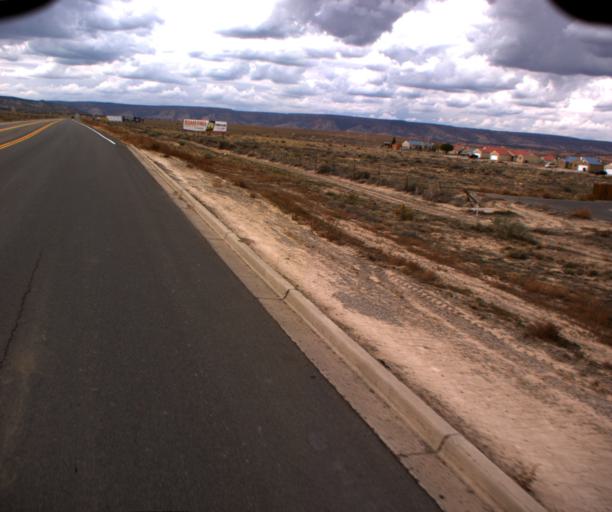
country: US
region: Arizona
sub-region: Navajo County
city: Kayenta
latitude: 36.7065
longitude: -110.2559
